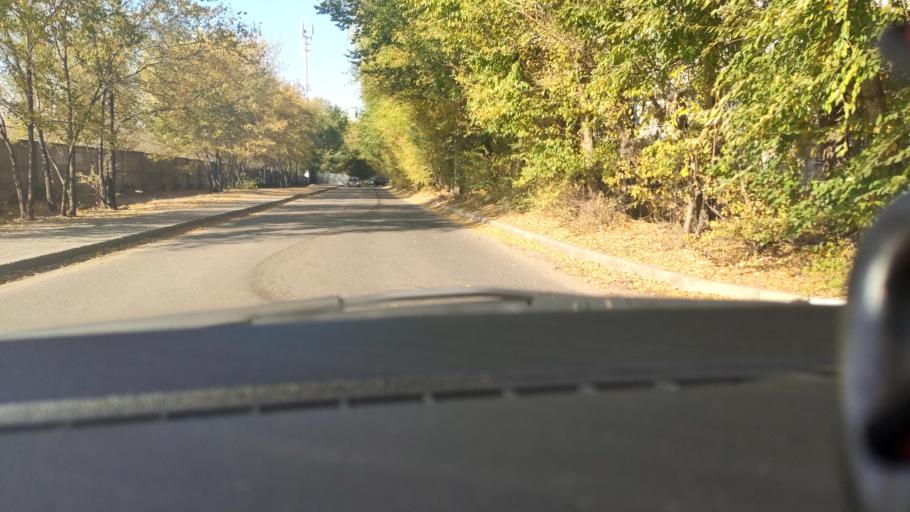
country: RU
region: Voronezj
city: Pridonskoy
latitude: 51.6229
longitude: 39.0693
